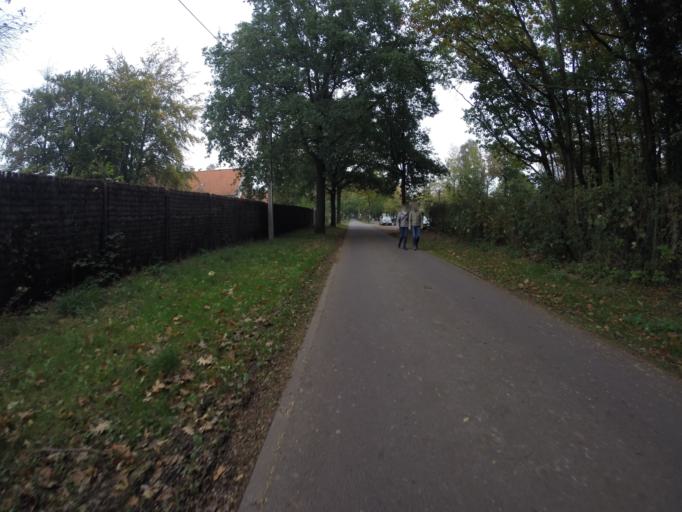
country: BE
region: Flanders
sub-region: Provincie West-Vlaanderen
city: Beernem
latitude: 51.0875
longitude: 3.3347
